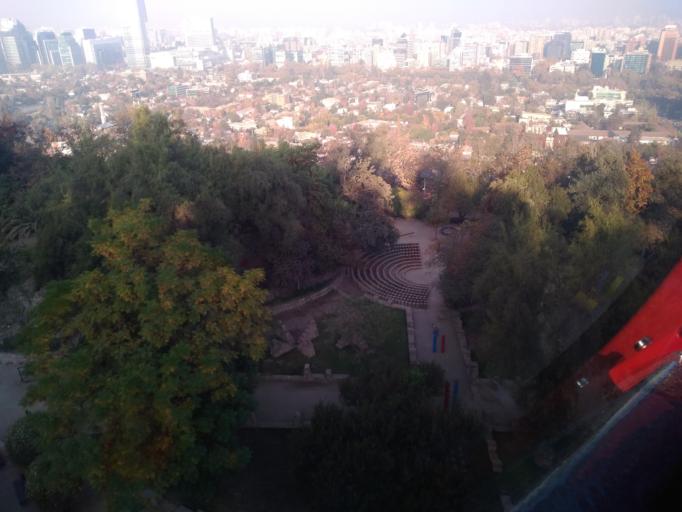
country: CL
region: Santiago Metropolitan
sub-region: Provincia de Santiago
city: Santiago
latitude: -33.4160
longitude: -70.6217
